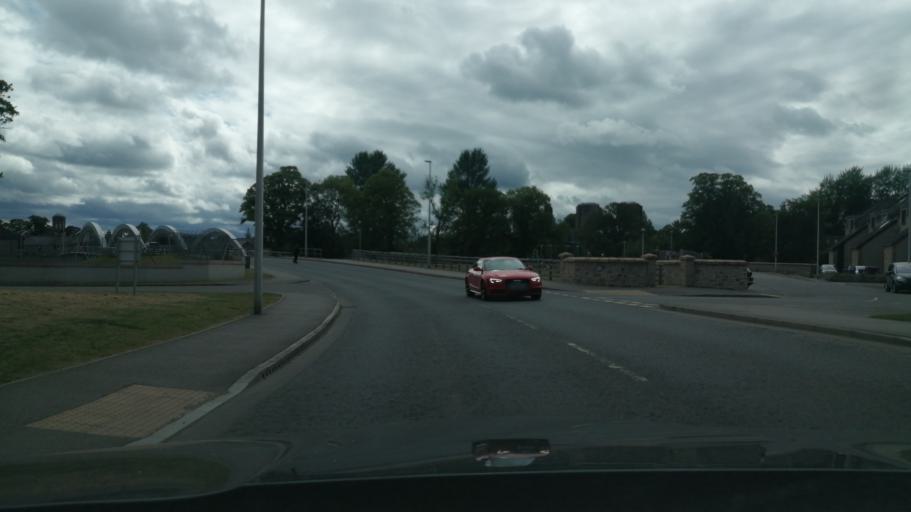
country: GB
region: Scotland
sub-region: Moray
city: Elgin
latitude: 57.6515
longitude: -3.3013
